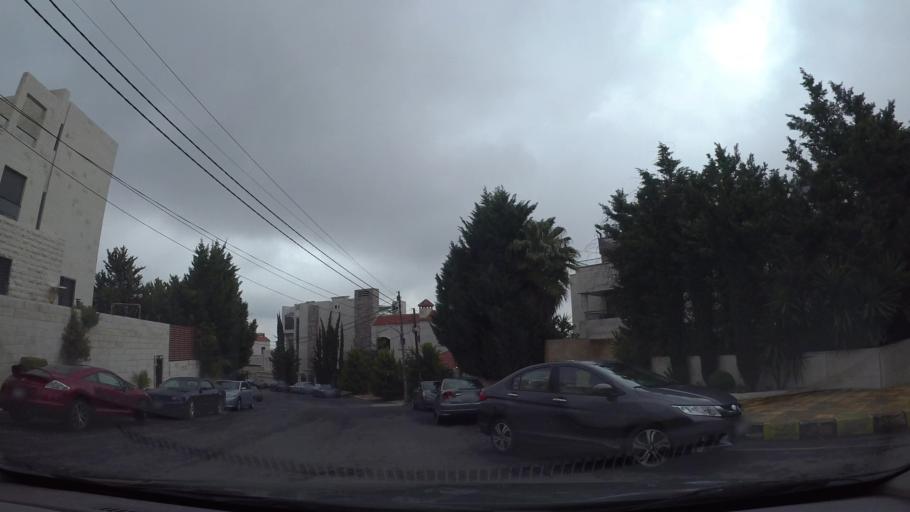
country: JO
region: Amman
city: Al Bunayyat ash Shamaliyah
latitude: 31.9336
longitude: 35.8916
